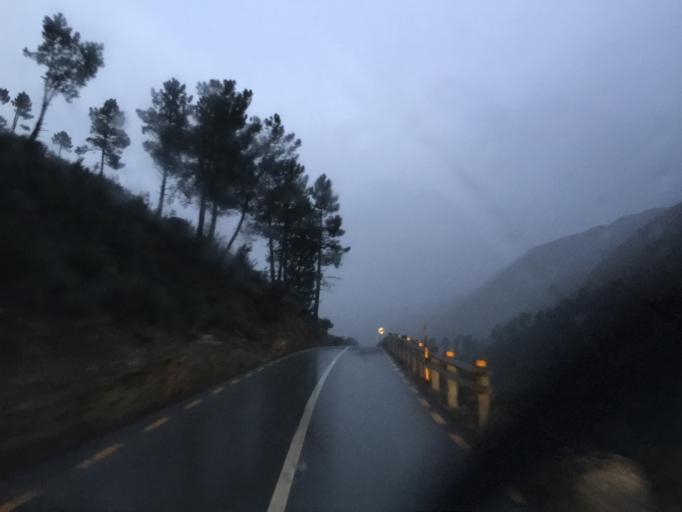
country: PT
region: Guarda
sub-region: Manteigas
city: Manteigas
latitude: 40.3625
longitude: -7.5539
